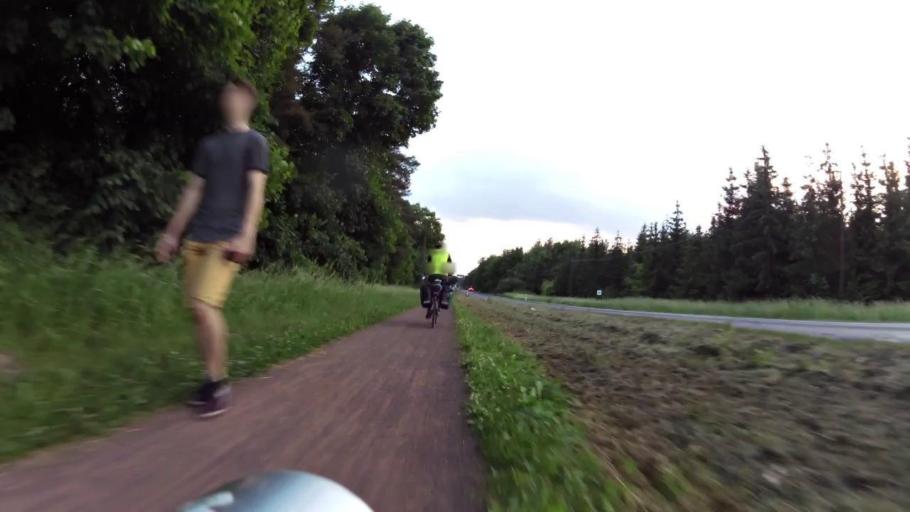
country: PL
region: Kujawsko-Pomorskie
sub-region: Bydgoszcz
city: Fordon
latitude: 53.1495
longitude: 18.2169
